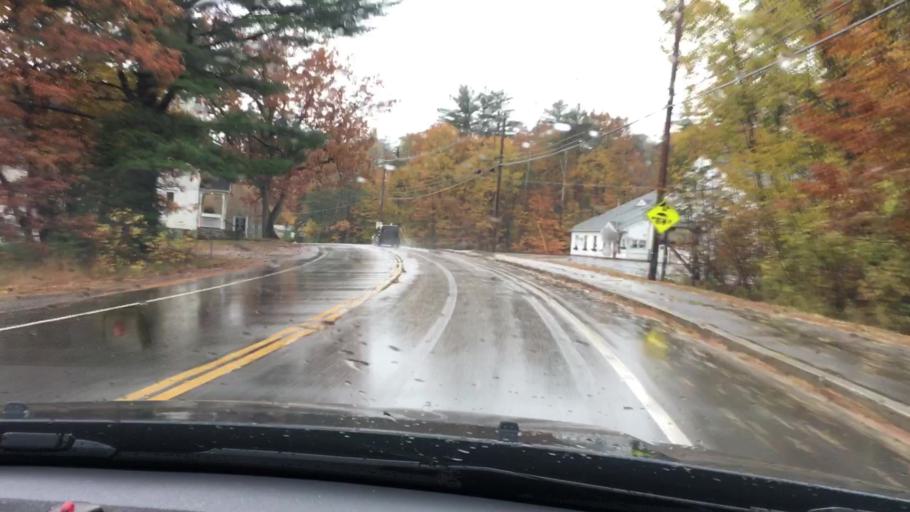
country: US
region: New Hampshire
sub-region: Grafton County
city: Holderness
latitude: 43.7313
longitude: -71.5919
